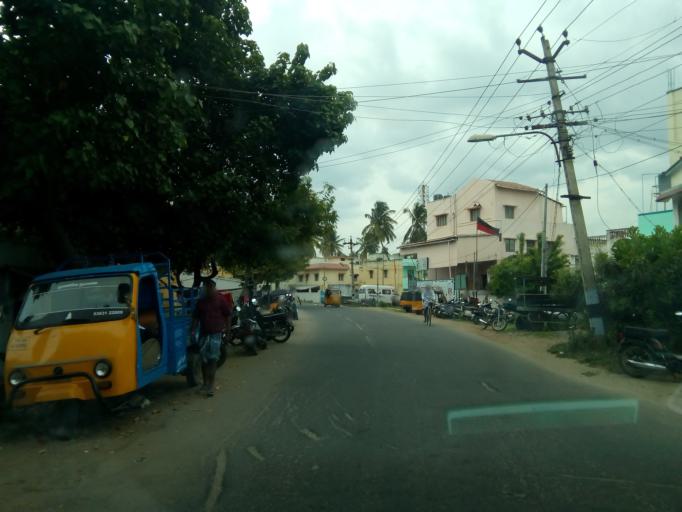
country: IN
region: Tamil Nadu
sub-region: Coimbatore
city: Coimbatore
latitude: 11.0058
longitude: 76.9427
